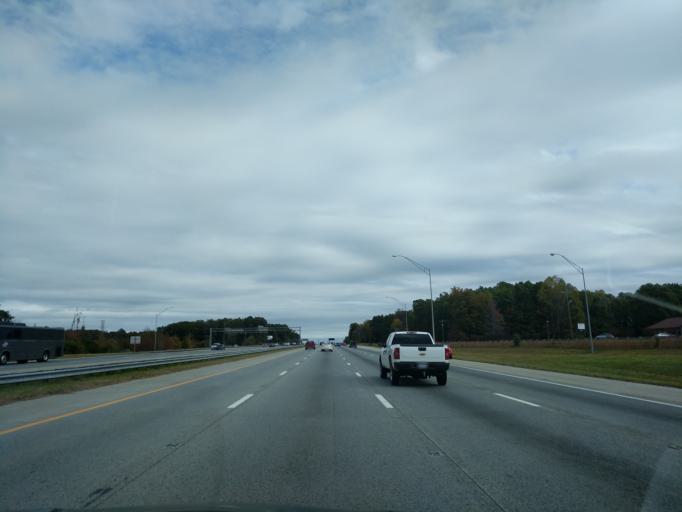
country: US
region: North Carolina
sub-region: Rowan County
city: Salisbury
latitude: 35.6198
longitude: -80.5074
